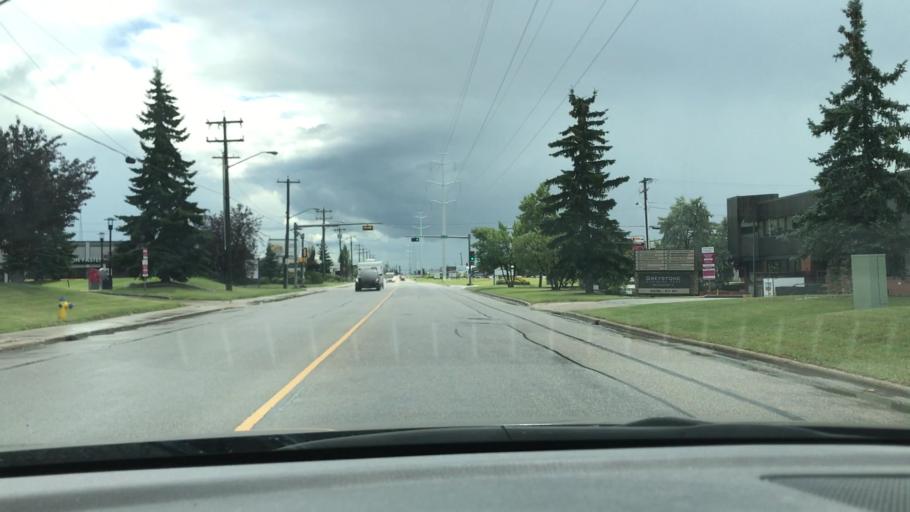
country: CA
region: Alberta
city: Edmonton
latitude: 53.4799
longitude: -113.4792
